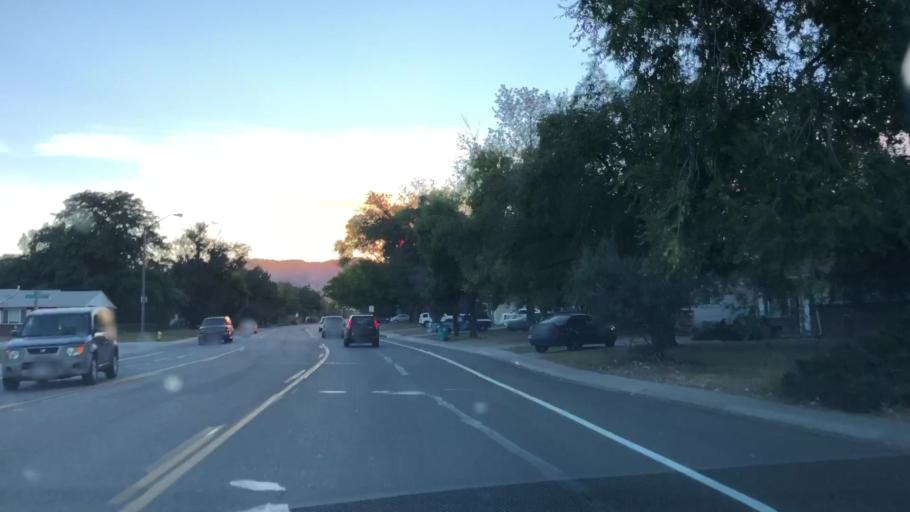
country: US
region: Colorado
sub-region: Larimer County
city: Fort Collins
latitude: 40.5748
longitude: -105.1103
